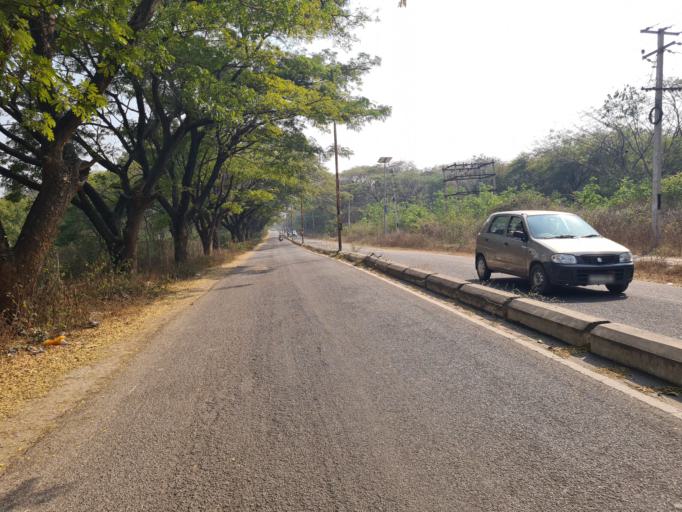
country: IN
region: Telangana
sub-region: Medak
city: Serilingampalle
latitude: 17.4897
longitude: 78.2979
